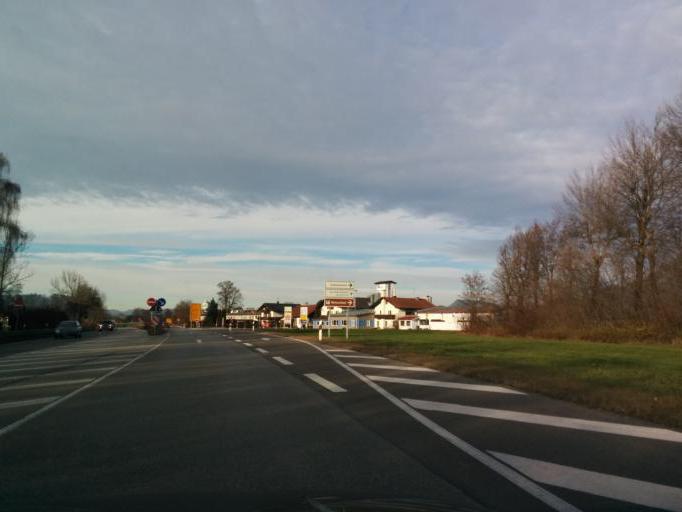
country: DE
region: Bavaria
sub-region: Swabia
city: Sonthofen
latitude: 47.5152
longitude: 10.2708
